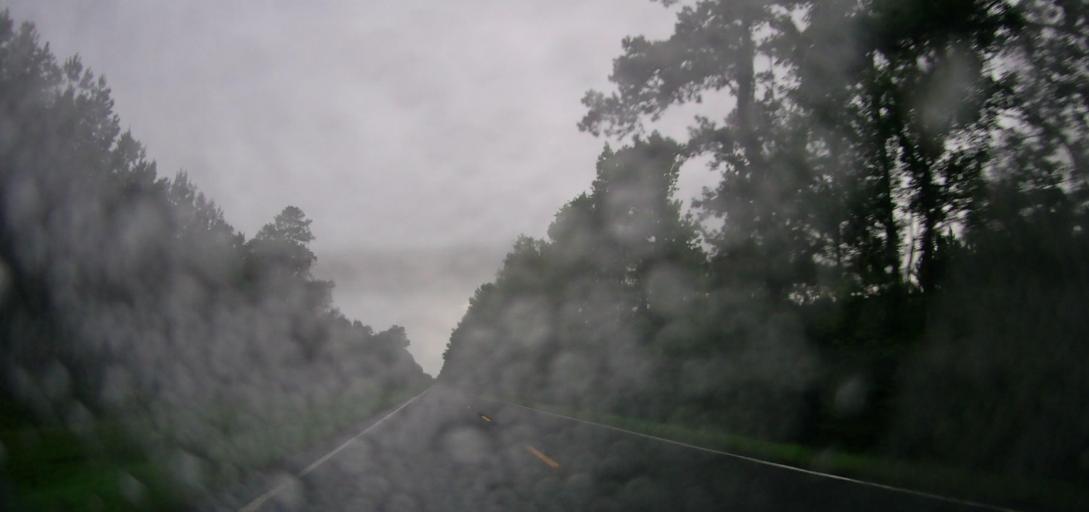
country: US
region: Georgia
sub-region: Glynn County
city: Dock Junction
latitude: 31.2723
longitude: -81.6469
